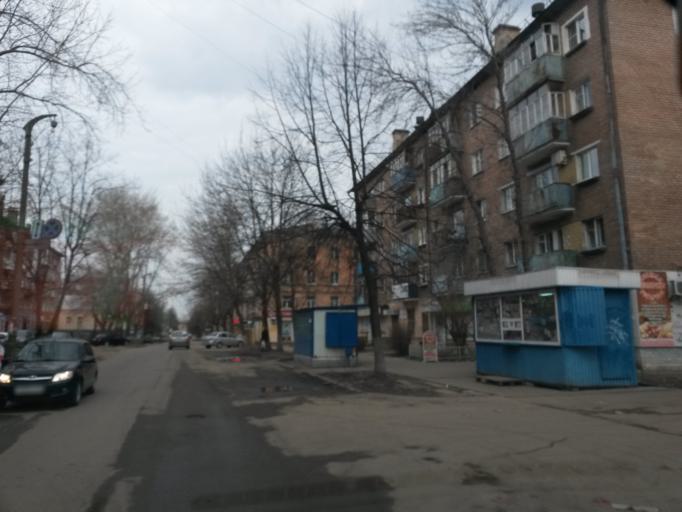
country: RU
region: Jaroslavl
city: Yaroslavl
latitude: 57.6279
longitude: 39.8607
